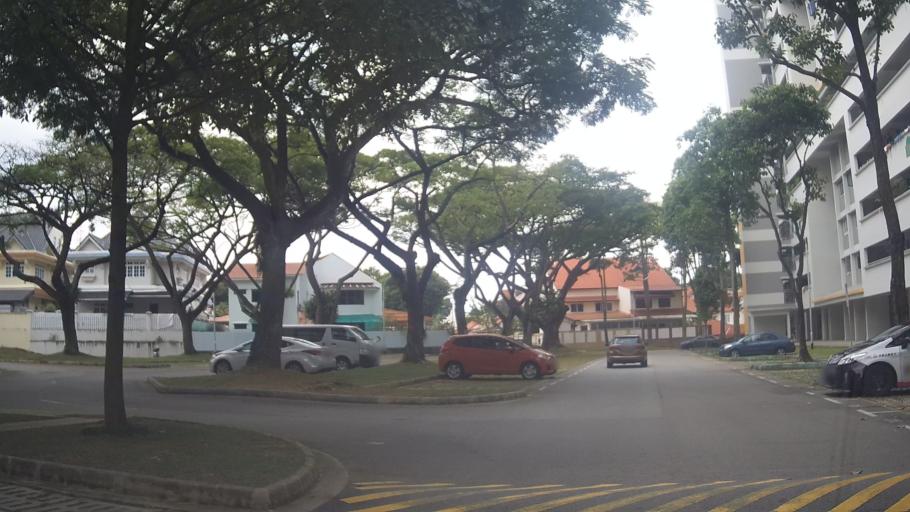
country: SG
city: Singapore
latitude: 1.3591
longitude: 103.8719
